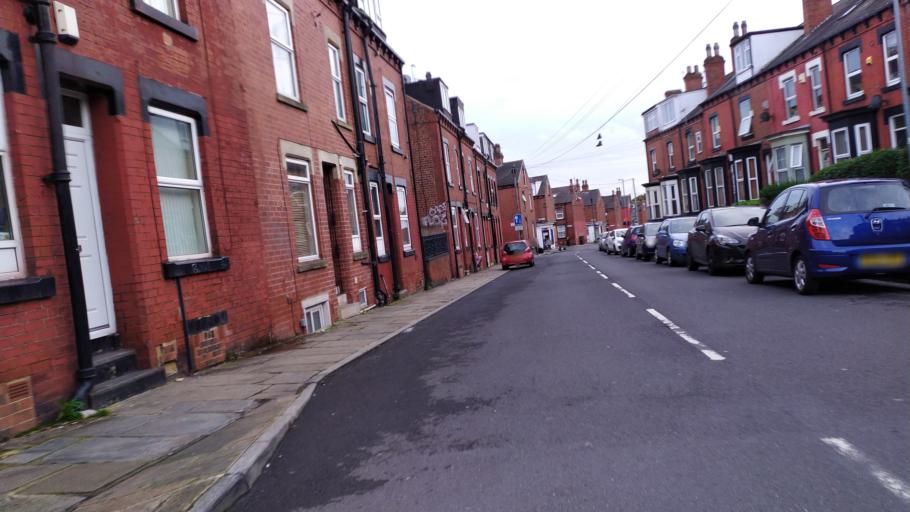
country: GB
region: England
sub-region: City and Borough of Leeds
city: Leeds
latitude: 53.8107
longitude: -1.5732
